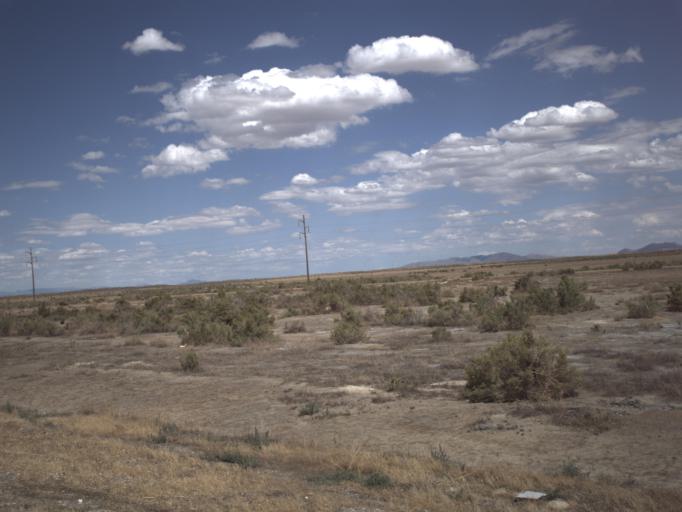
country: US
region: Utah
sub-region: Millard County
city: Delta
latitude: 39.2885
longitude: -112.4648
